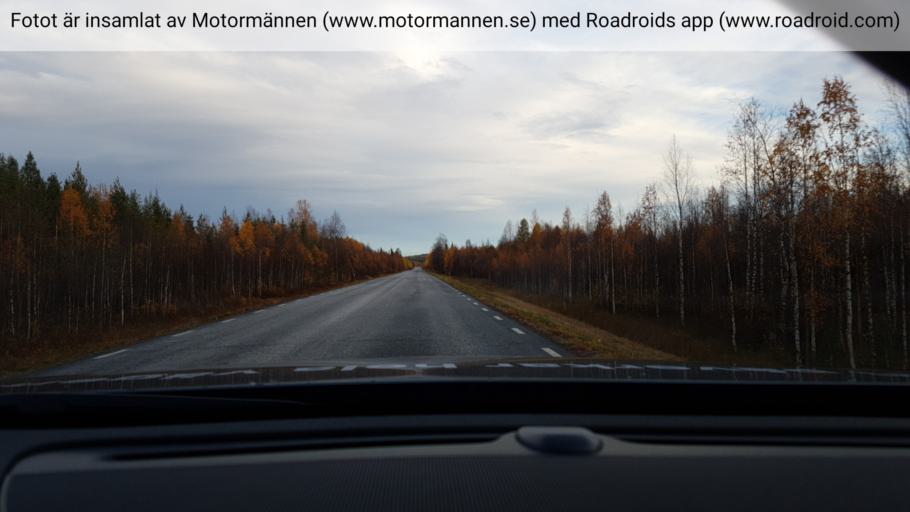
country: SE
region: Norrbotten
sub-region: Overkalix Kommun
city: OEverkalix
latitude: 66.9240
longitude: 22.7432
